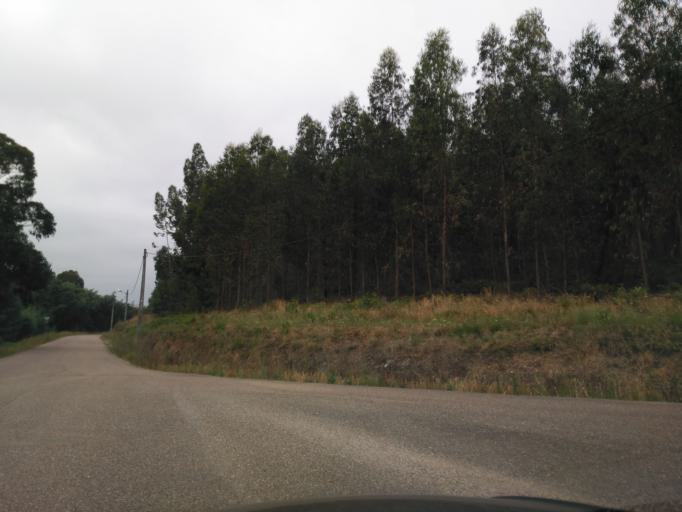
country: PT
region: Santarem
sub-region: Abrantes
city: Alferrarede
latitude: 39.5569
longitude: -8.1452
